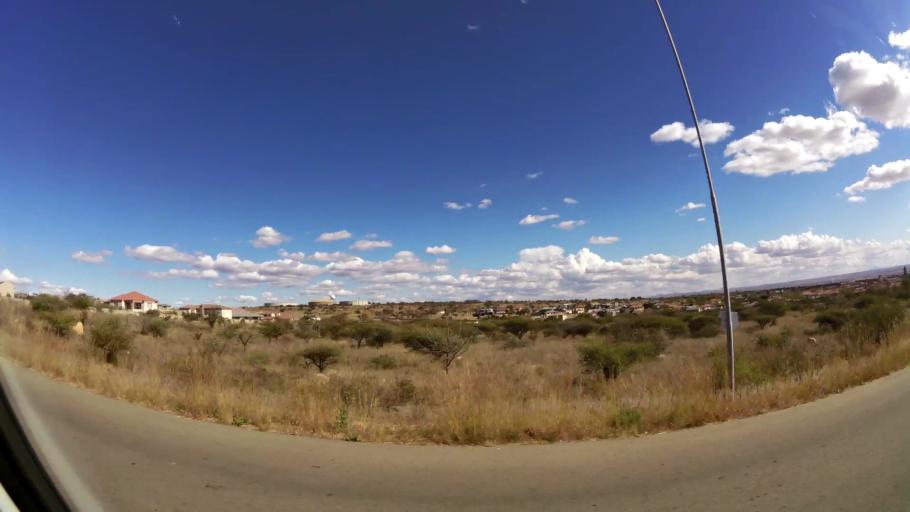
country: ZA
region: Limpopo
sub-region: Capricorn District Municipality
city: Polokwane
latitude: -23.8852
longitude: 29.5122
